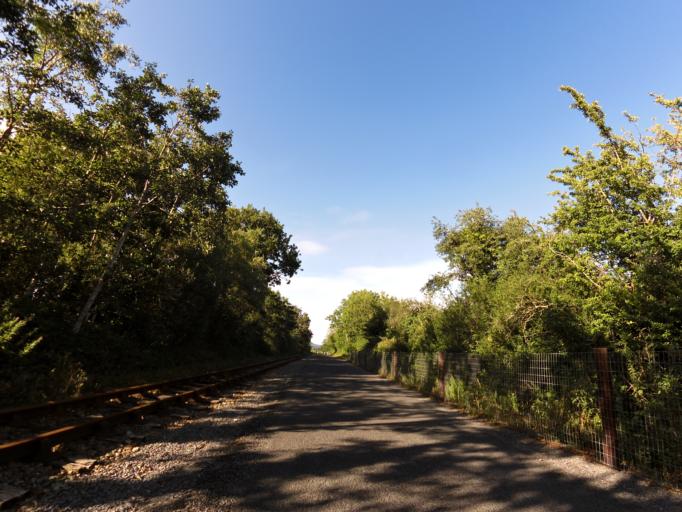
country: IE
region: Leinster
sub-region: Kilkenny
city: Mooncoin
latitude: 52.2530
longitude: -7.1931
